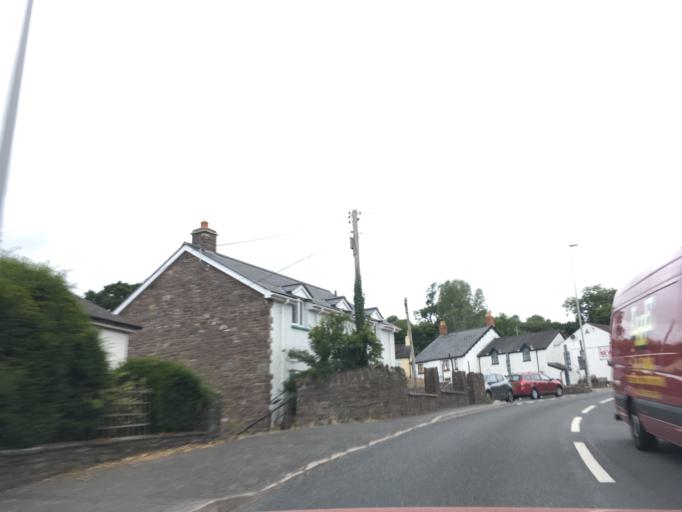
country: GB
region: Wales
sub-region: Blaenau Gwent
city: Brynmawr
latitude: 51.8900
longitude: -3.2368
